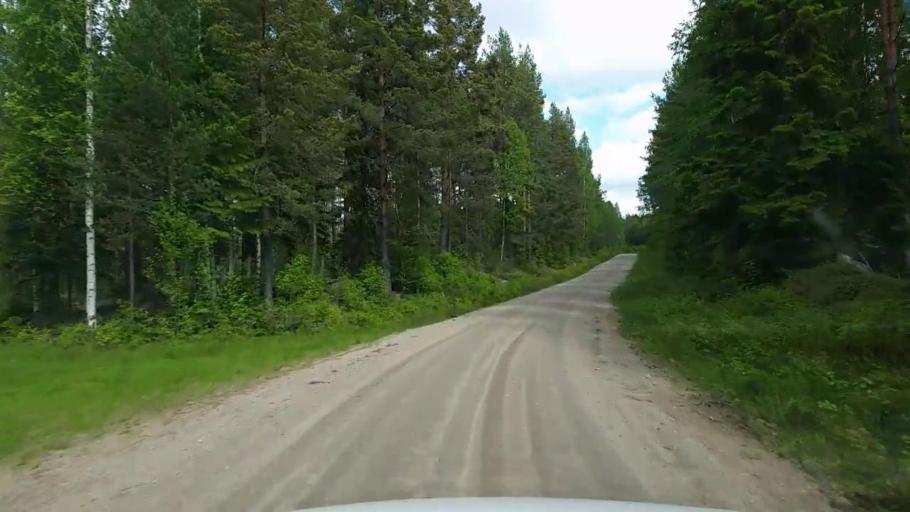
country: SE
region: Gaevleborg
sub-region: Ovanakers Kommun
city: Edsbyn
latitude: 61.5265
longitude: 15.9343
